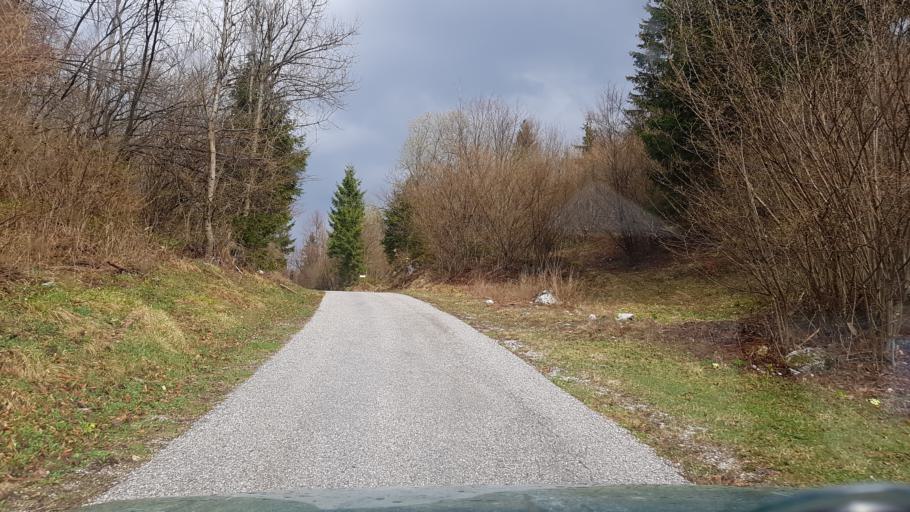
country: SI
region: Cerkno
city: Cerkno
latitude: 46.1367
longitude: 13.8792
